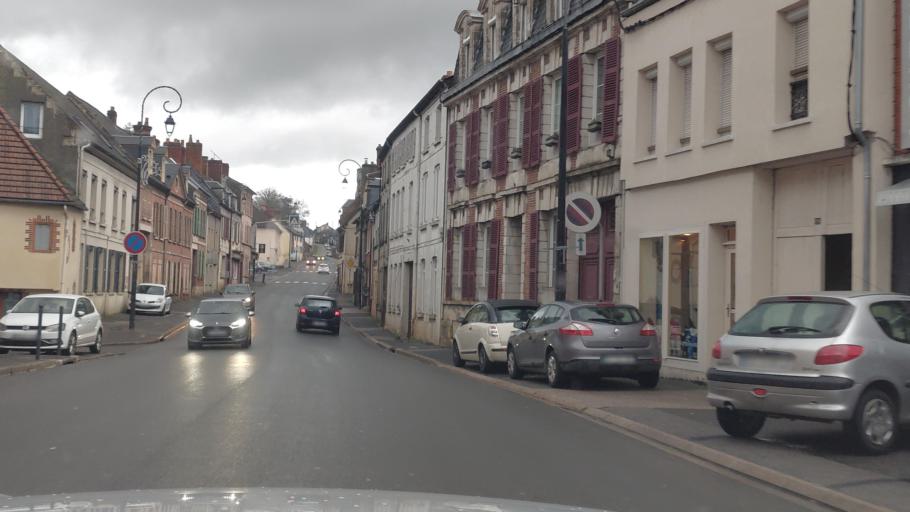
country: FR
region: Picardie
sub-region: Departement de l'Oise
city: Saint-Omer-en-Chaussee
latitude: 49.5744
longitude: 1.9561
